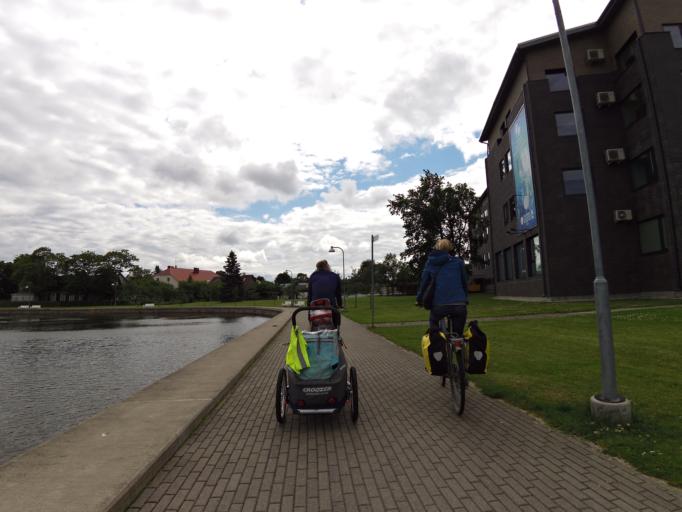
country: EE
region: Laeaene
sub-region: Haapsalu linn
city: Haapsalu
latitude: 58.9525
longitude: 23.5332
